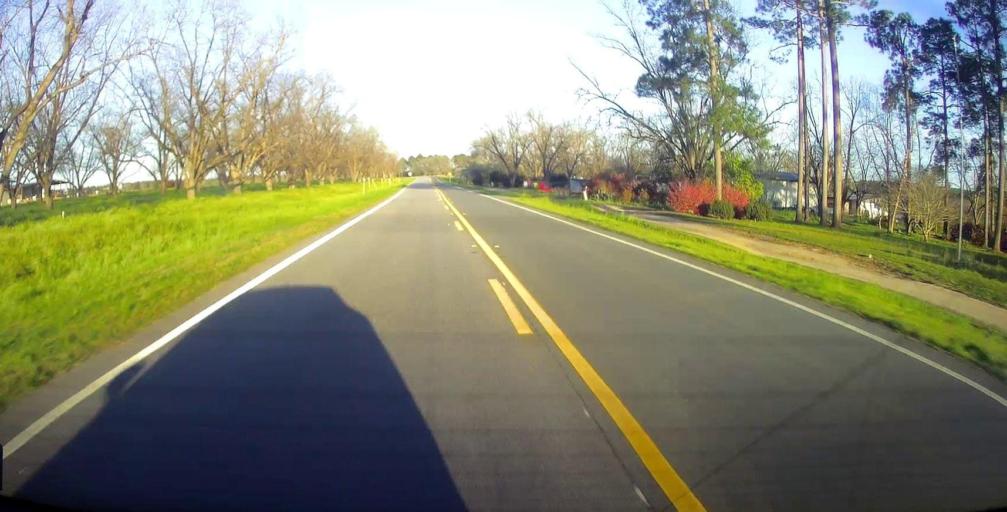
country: US
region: Georgia
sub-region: Wilcox County
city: Rochelle
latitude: 31.9609
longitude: -83.4072
